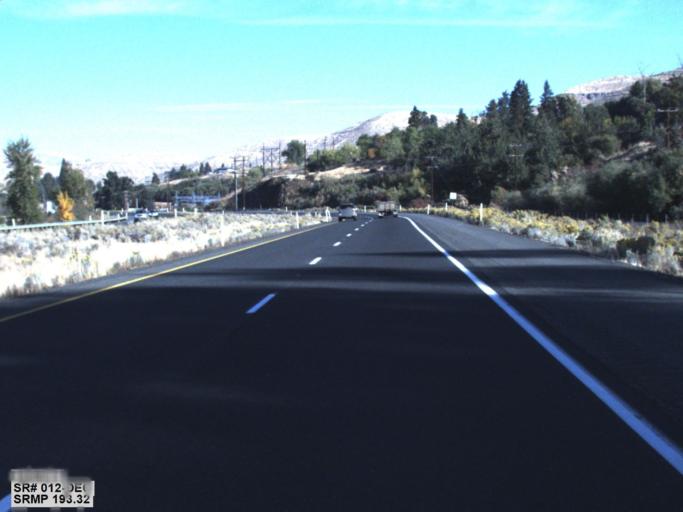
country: US
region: Washington
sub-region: Yakima County
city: Gleed
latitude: 46.6926
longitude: -120.6528
